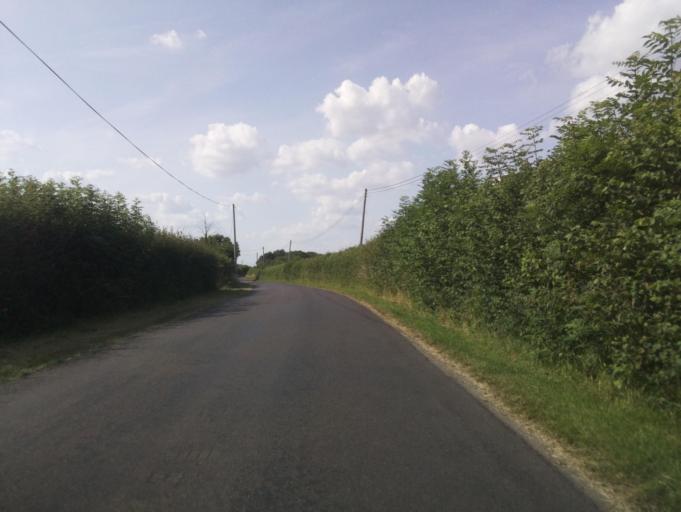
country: GB
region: England
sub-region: Wiltshire
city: Minety
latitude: 51.6294
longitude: -1.9735
